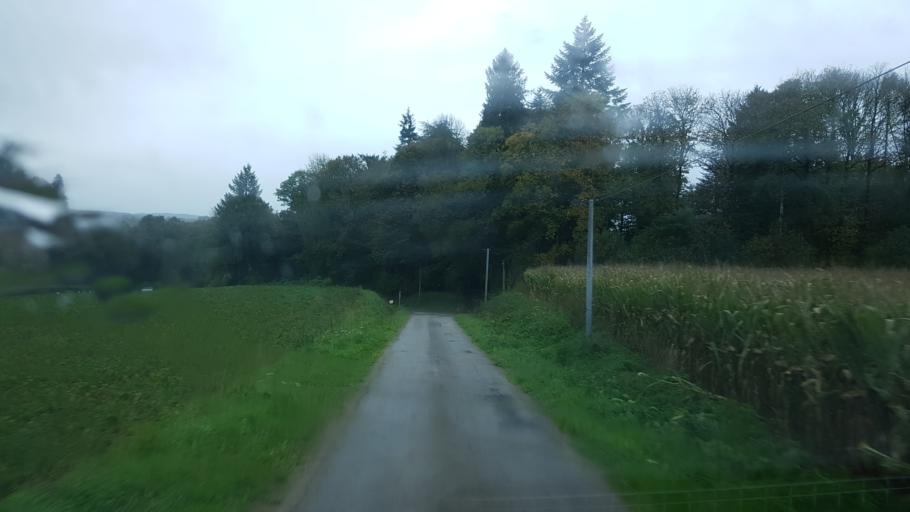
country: FR
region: Brittany
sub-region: Departement du Morbihan
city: Elven
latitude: 47.7462
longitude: -2.5478
